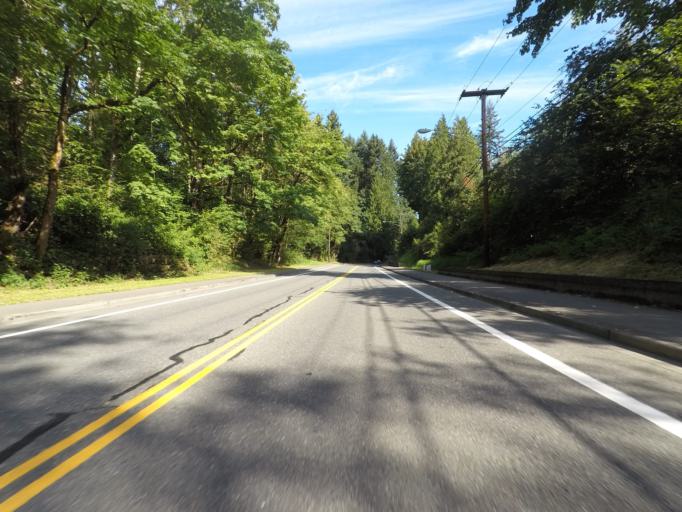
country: US
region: Washington
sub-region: King County
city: Bothell
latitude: 47.7432
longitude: -122.2115
